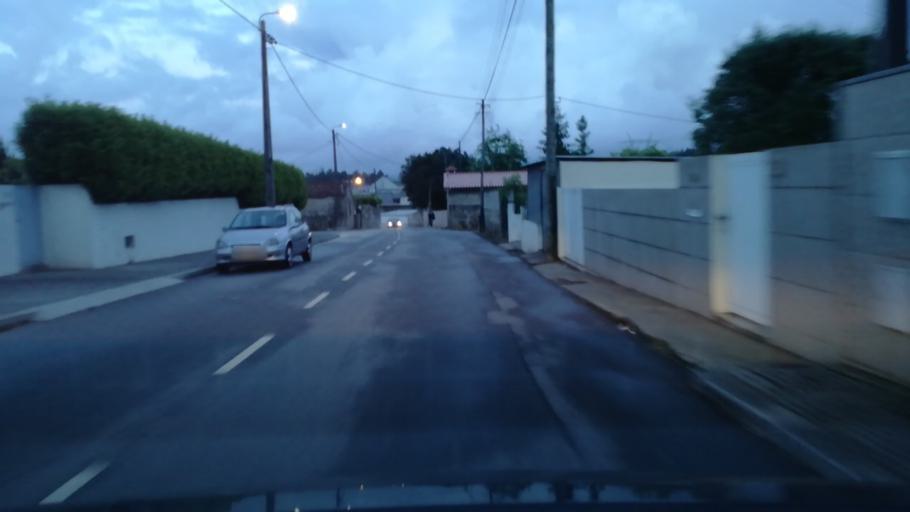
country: PT
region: Porto
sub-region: Maia
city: Maia
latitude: 41.2506
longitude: -8.6248
